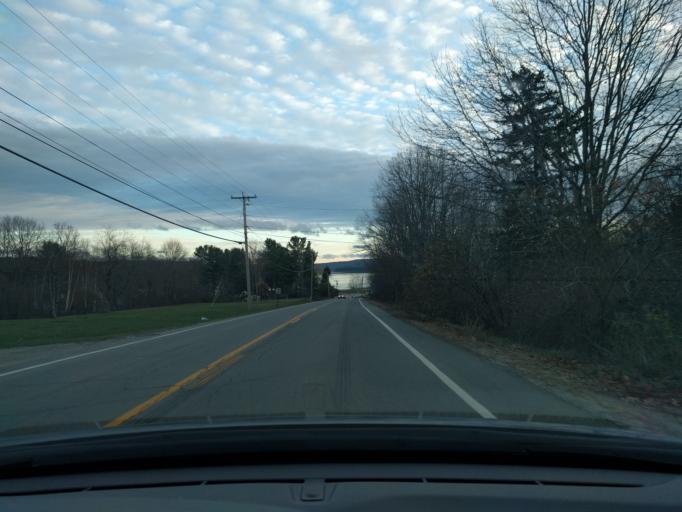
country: US
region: Maine
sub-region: Waldo County
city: Winterport
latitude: 44.6357
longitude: -68.8497
